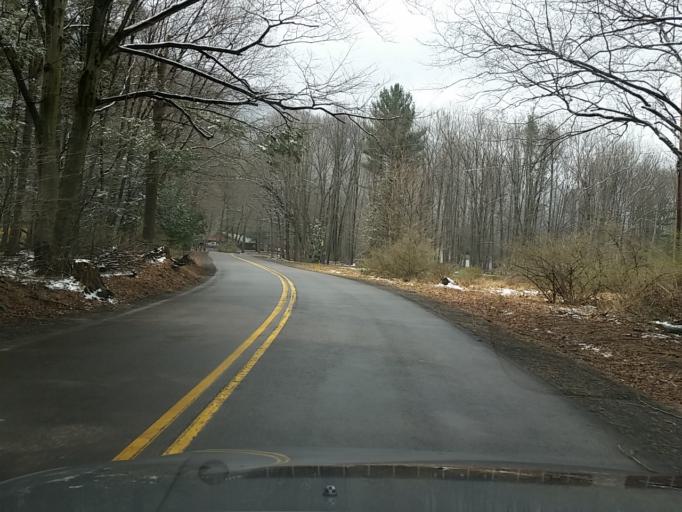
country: US
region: Pennsylvania
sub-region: Sullivan County
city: Laporte
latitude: 41.3003
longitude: -76.3809
